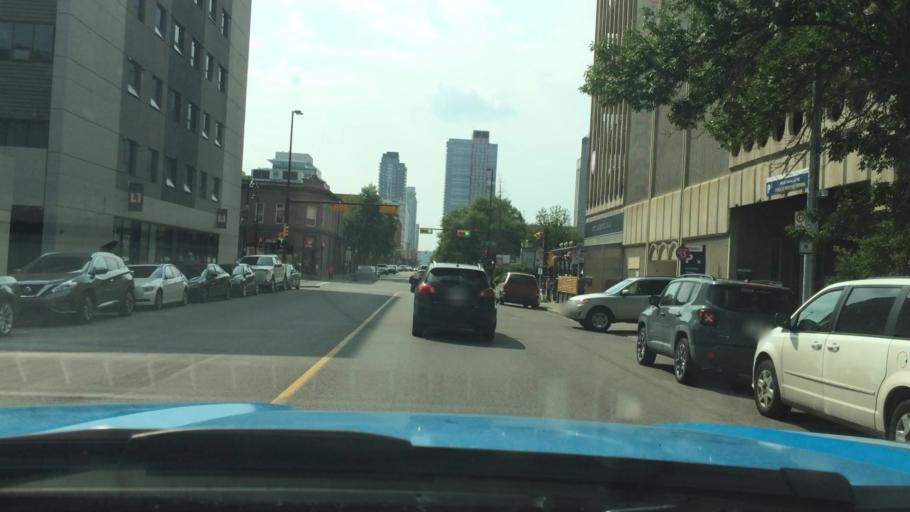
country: CA
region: Alberta
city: Calgary
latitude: 51.0434
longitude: -114.0645
